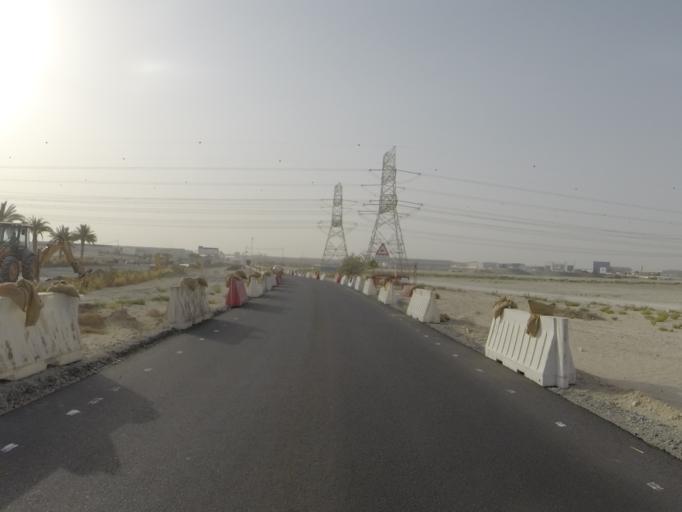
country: AE
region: Dubai
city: Dubai
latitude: 24.9562
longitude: 55.1034
